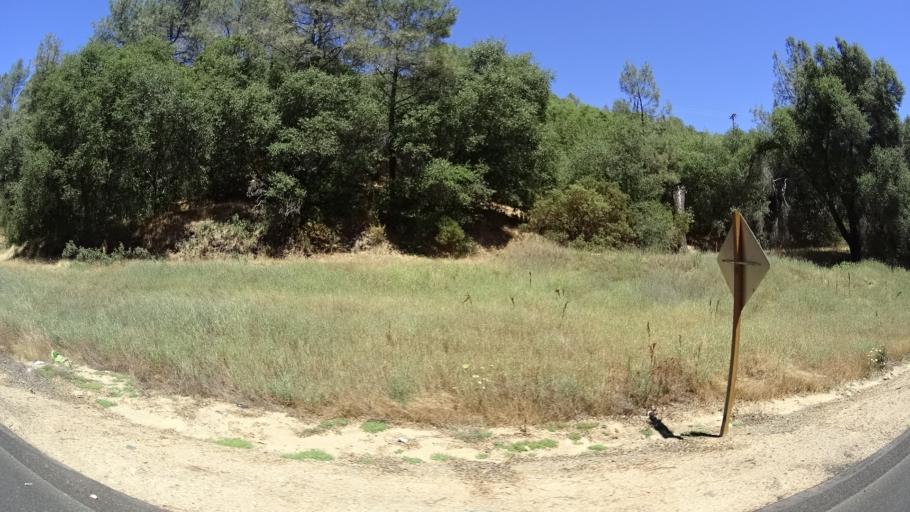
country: US
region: California
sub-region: Calaveras County
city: San Andreas
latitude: 38.2655
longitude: -120.7155
